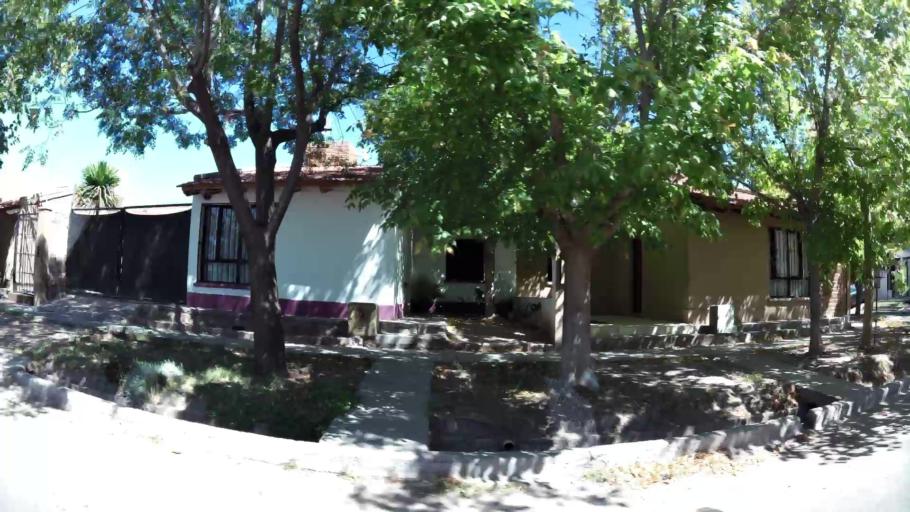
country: AR
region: Mendoza
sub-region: Departamento de Godoy Cruz
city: Godoy Cruz
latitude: -32.9777
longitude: -68.8484
